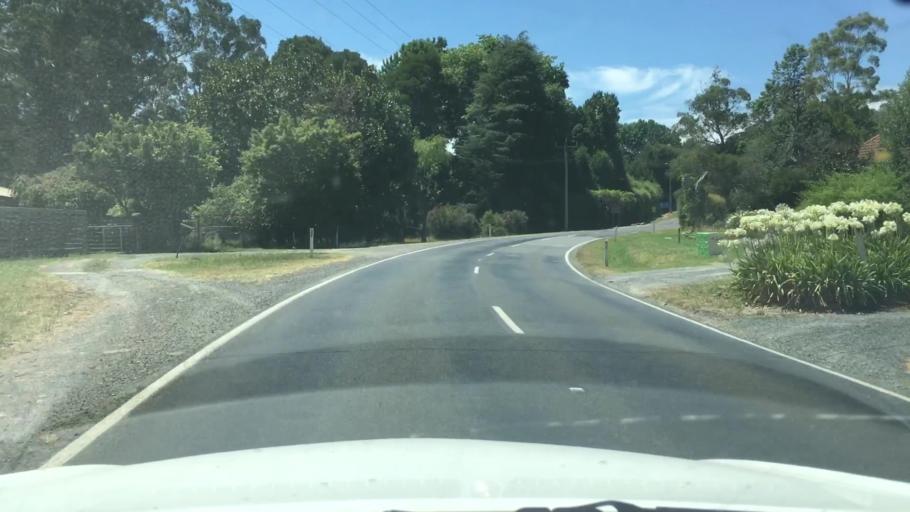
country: AU
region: Victoria
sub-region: Yarra Ranges
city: Millgrove
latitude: -37.7439
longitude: 145.7324
